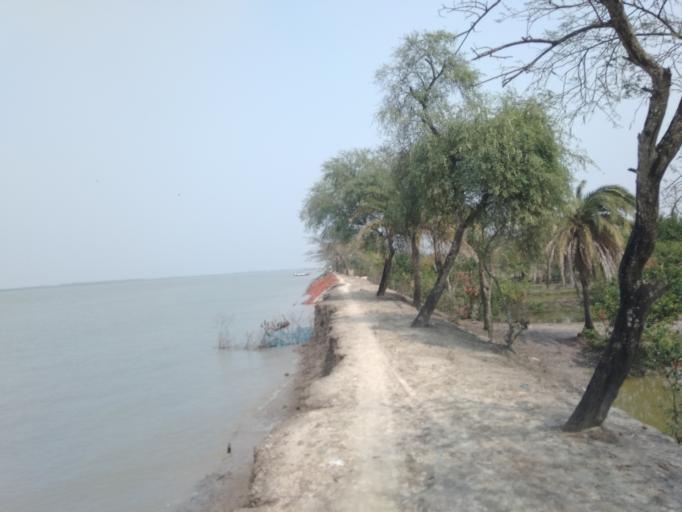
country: IN
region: West Bengal
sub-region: North 24 Parganas
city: Gosaba
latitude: 22.2502
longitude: 89.2502
